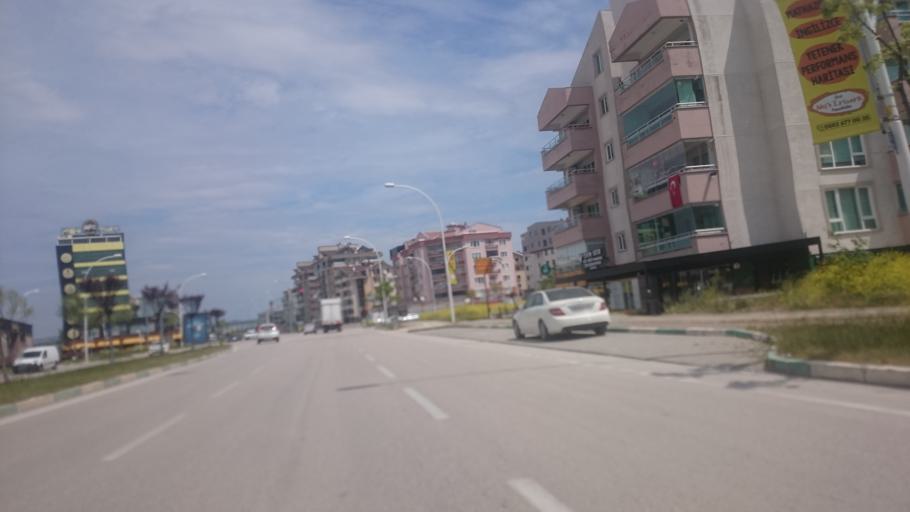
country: TR
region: Bursa
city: Cali
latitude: 40.2279
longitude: 28.9155
